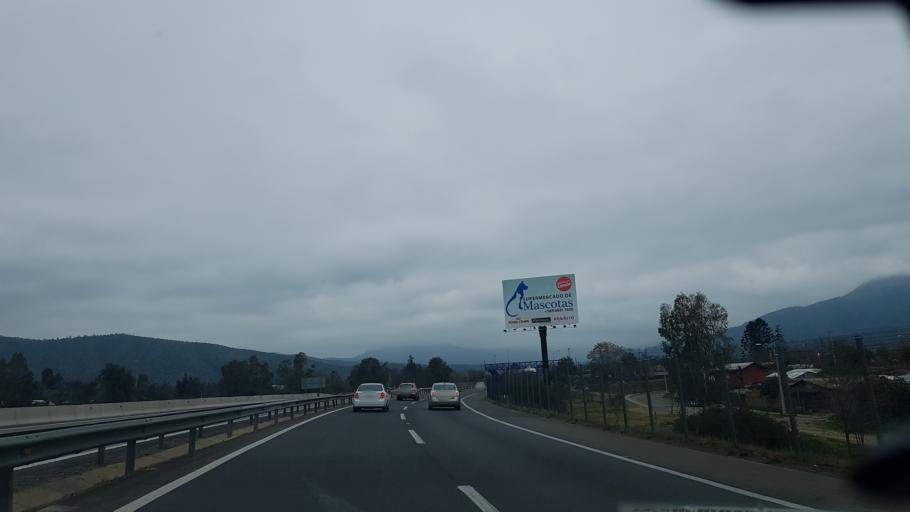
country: CL
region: Santiago Metropolitan
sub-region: Provincia de Melipilla
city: Melipilla
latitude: -33.4132
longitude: -71.1515
